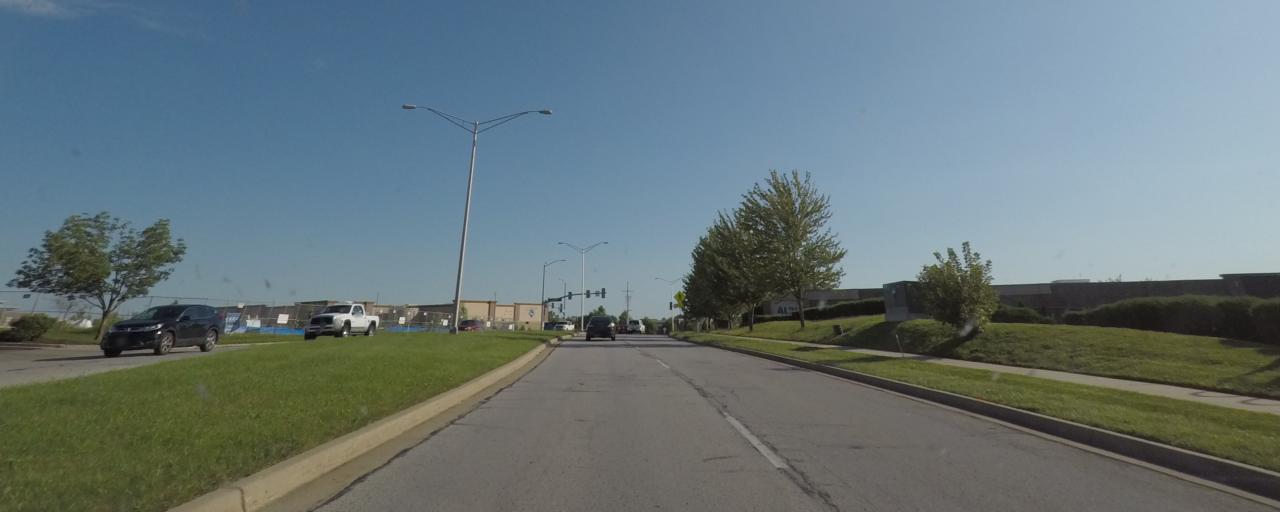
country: US
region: Missouri
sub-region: Clay County
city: Pleasant Valley
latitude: 39.2432
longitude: -94.4654
